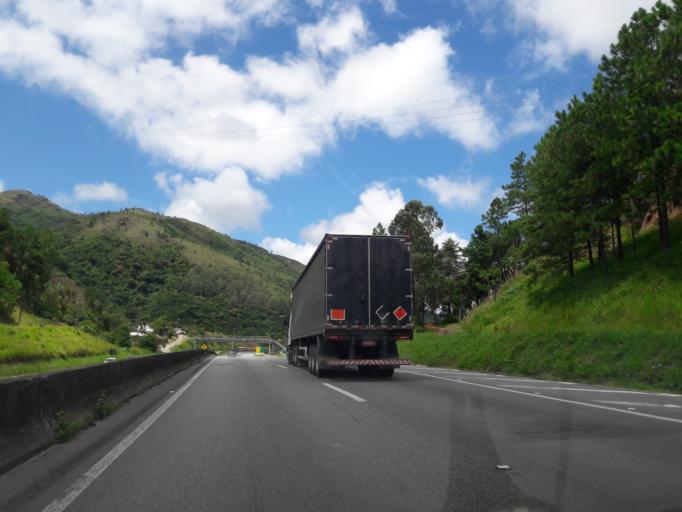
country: BR
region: Parana
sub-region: Campina Grande Do Sul
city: Campina Grande do Sul
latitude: -25.1369
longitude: -48.8571
